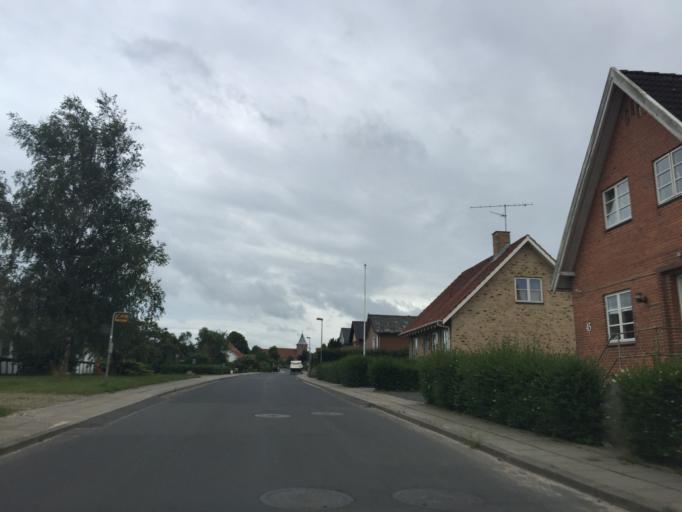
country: DK
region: Central Jutland
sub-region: Silkeborg Kommune
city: Silkeborg
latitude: 56.2392
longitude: 9.5466
